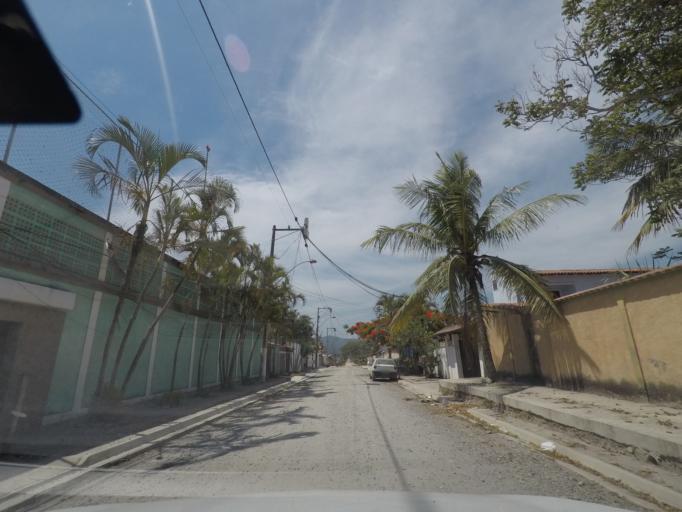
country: BR
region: Rio de Janeiro
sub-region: Marica
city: Marica
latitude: -22.9659
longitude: -42.9550
